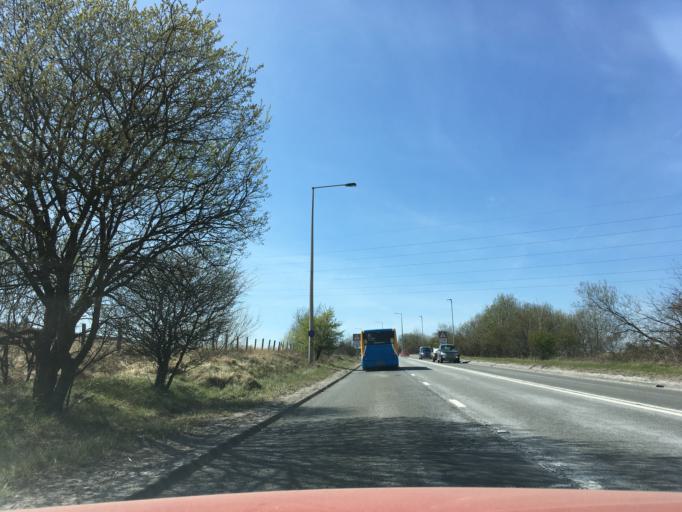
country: GB
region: Wales
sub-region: Rhondda Cynon Taf
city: Aberdare
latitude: 51.7562
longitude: -3.4348
